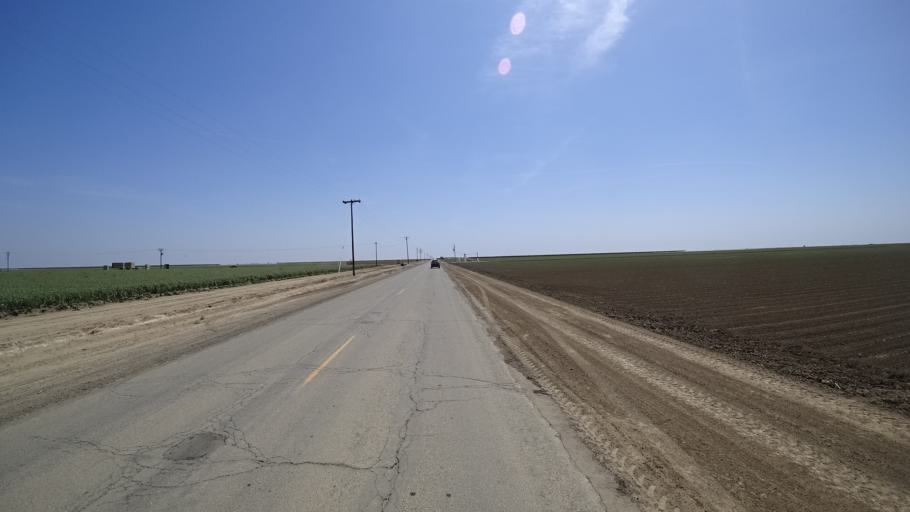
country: US
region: California
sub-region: Kings County
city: Kettleman City
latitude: 36.1377
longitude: -119.9793
